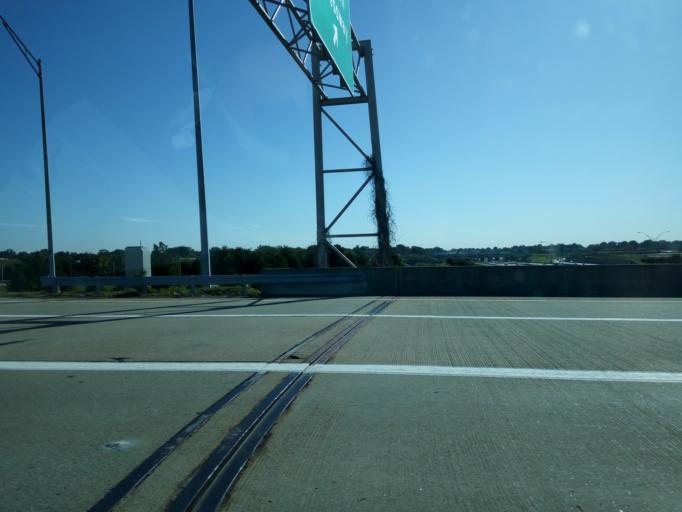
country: US
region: Kentucky
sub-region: Jefferson County
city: Audubon Park
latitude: 38.1904
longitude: -85.7383
